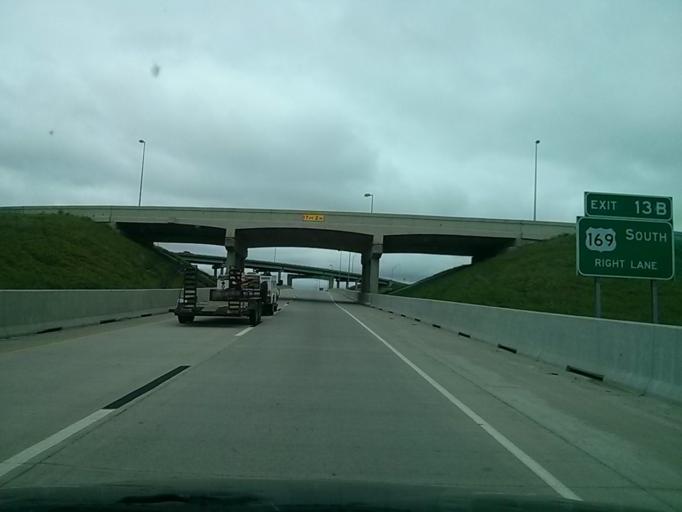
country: US
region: Oklahoma
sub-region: Tulsa County
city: Owasso
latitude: 36.1661
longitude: -95.8581
